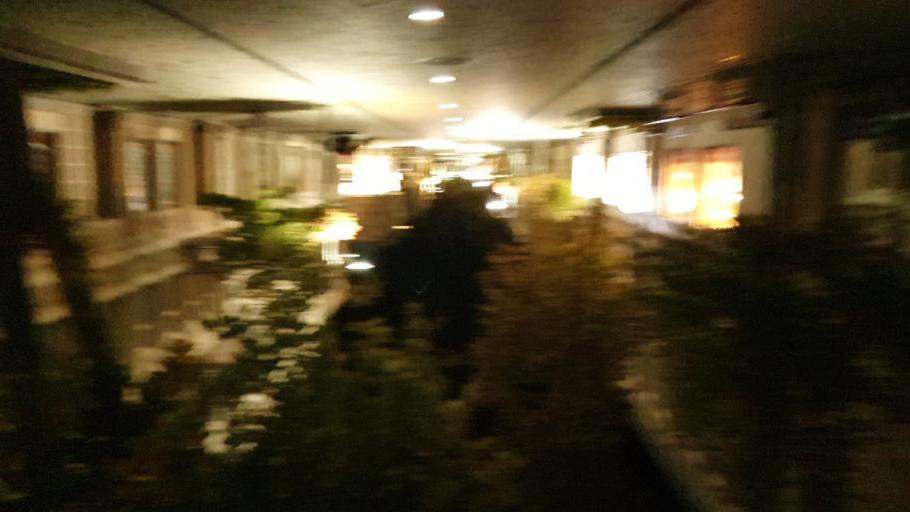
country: LV
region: Daugavpils
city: Daugavpils
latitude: 55.8741
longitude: 26.5253
